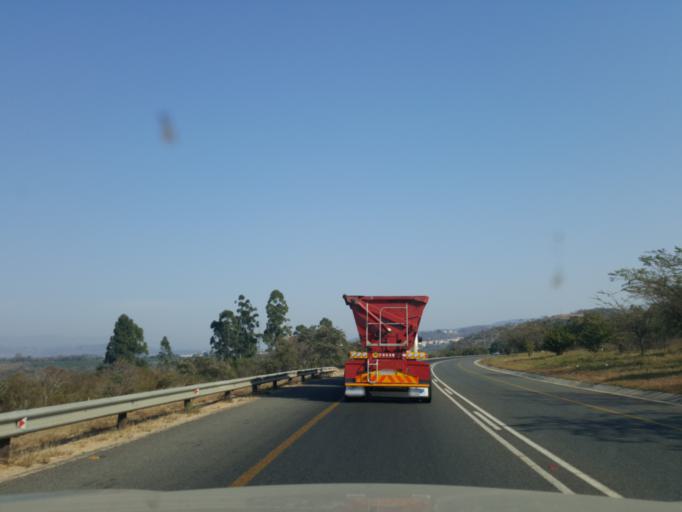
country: ZA
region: Mpumalanga
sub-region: Ehlanzeni District
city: Nelspruit
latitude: -25.4465
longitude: 30.9887
